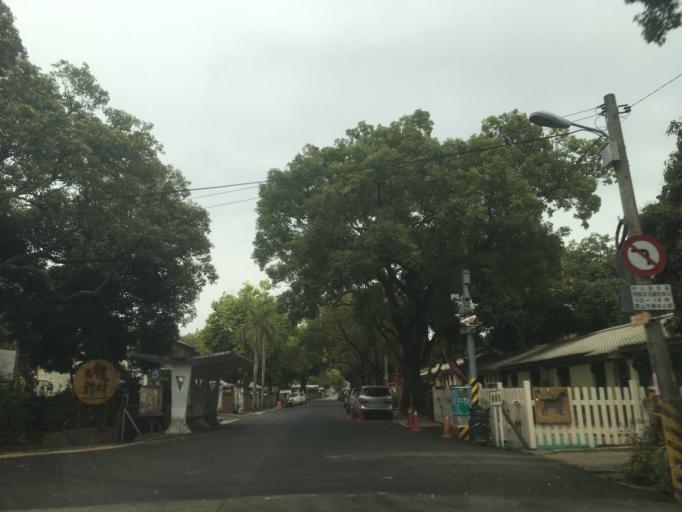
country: TW
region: Taiwan
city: Zhongxing New Village
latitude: 24.0432
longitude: 120.6948
